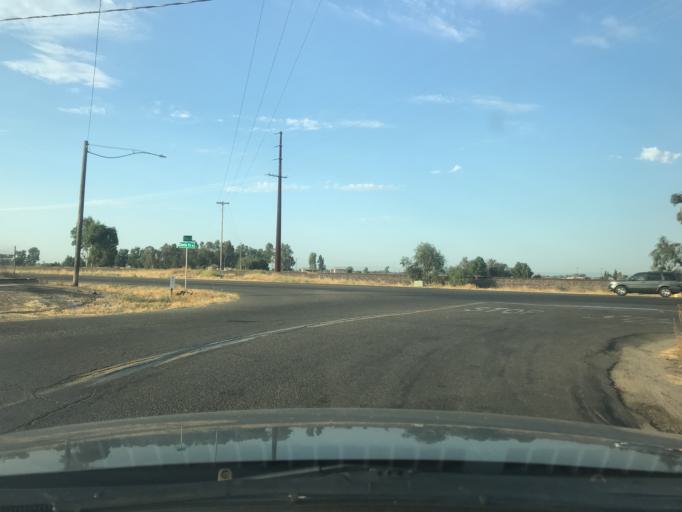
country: US
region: California
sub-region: Merced County
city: Atwater
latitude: 37.3465
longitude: -120.5496
